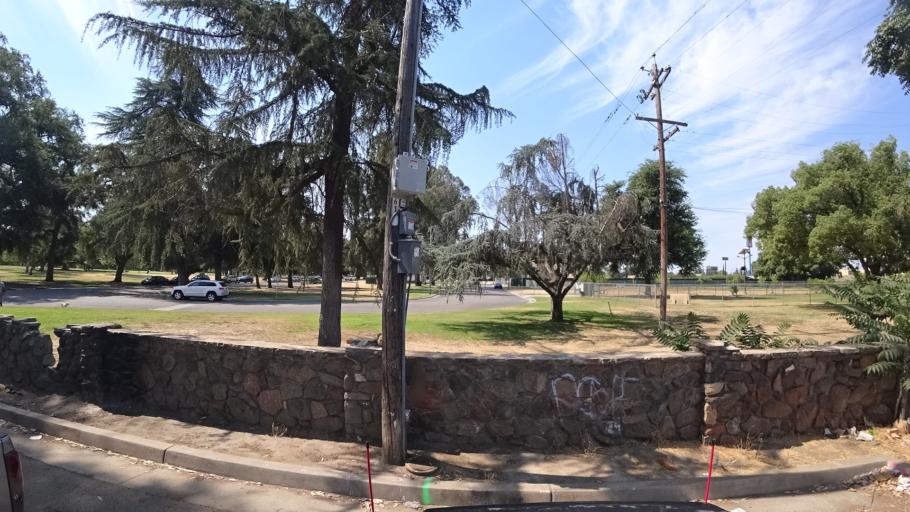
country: US
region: California
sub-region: Fresno County
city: West Park
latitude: 36.7557
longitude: -119.8267
